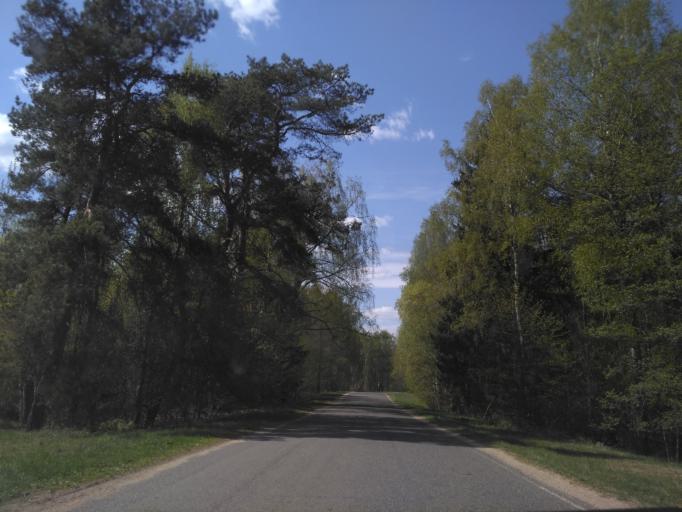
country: BY
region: Minsk
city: Narach
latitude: 54.9628
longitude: 26.6450
